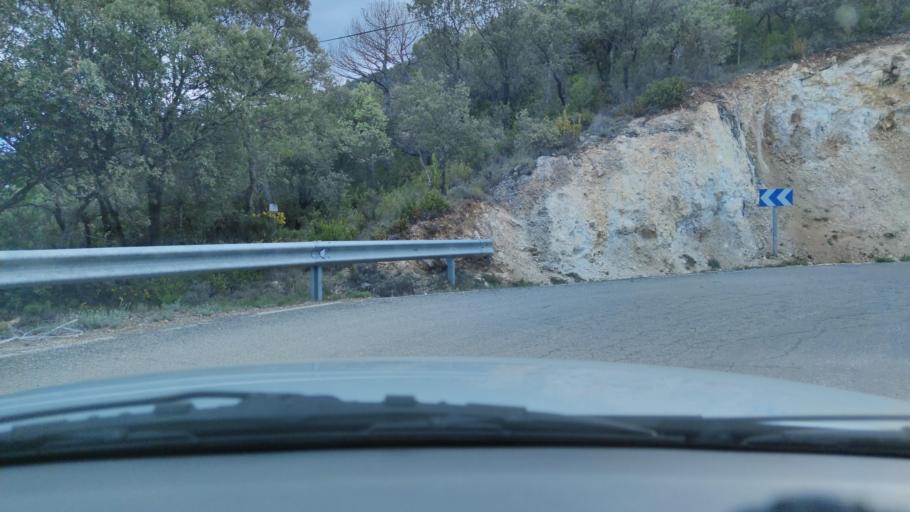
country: ES
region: Catalonia
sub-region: Provincia de Lleida
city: Coll de Nargo
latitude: 42.2490
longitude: 1.3578
